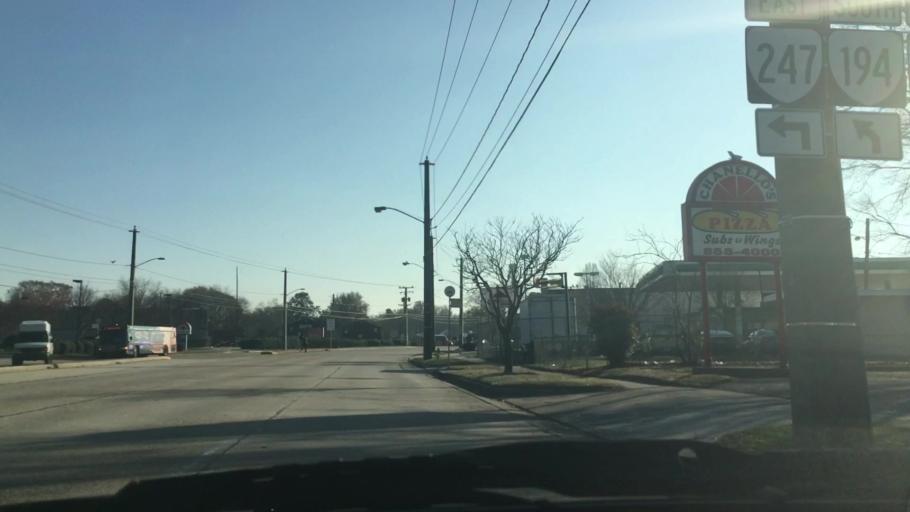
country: US
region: Virginia
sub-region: City of Norfolk
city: Norfolk
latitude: 36.8920
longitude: -76.2380
